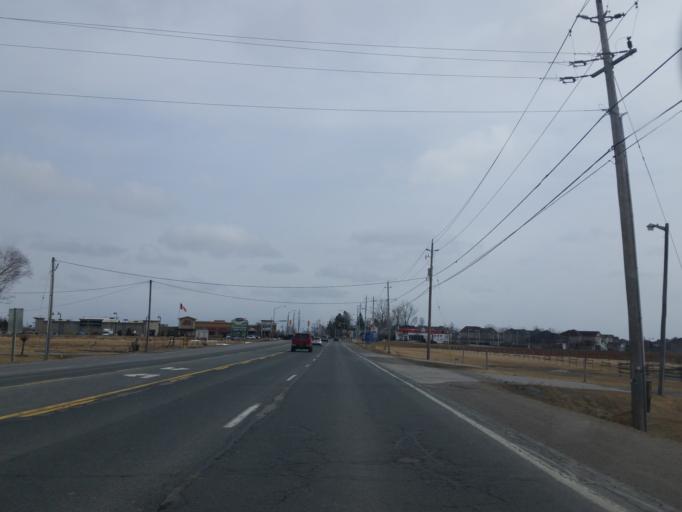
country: CA
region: Ontario
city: Oshawa
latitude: 43.9100
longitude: -78.7204
